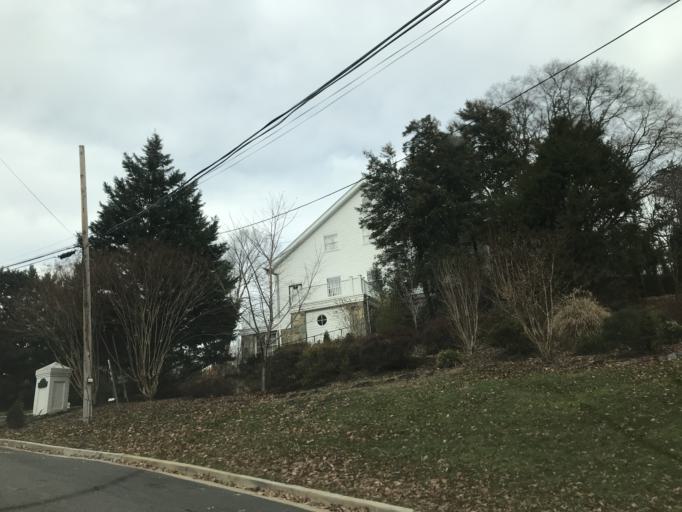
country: US
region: Virginia
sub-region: Arlington County
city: Arlington
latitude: 38.9008
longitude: -77.0870
